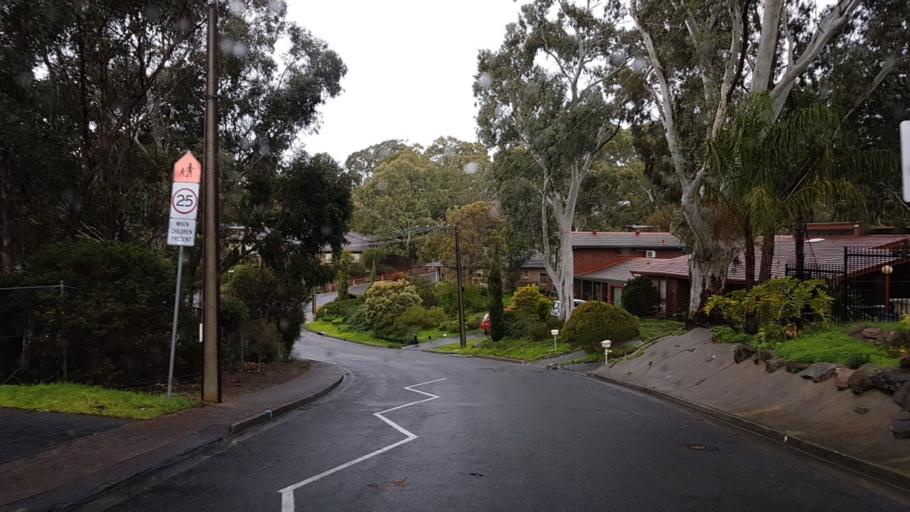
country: AU
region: South Australia
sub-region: Onkaparinga
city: Bedford Park
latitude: -35.0474
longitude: 138.5808
